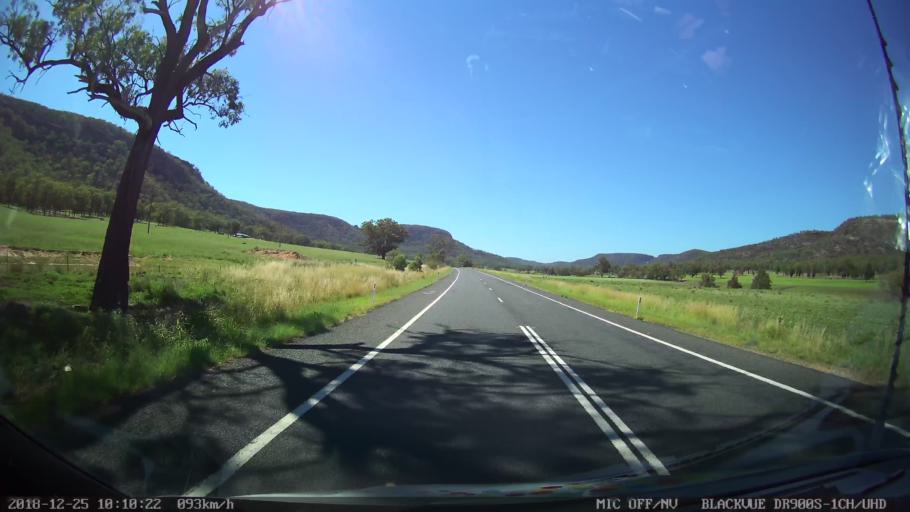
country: AU
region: New South Wales
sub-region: Muswellbrook
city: Denman
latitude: -32.3029
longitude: 150.5215
